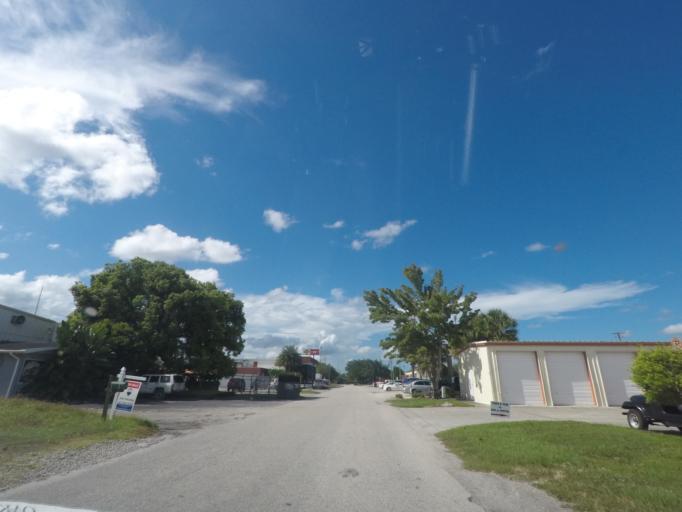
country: US
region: Florida
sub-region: Orange County
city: Fairview Shores
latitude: 28.5896
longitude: -81.3707
